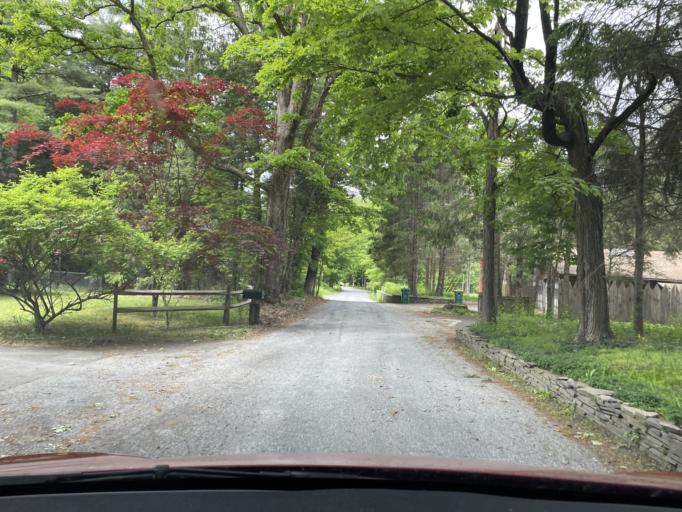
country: US
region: New York
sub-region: Ulster County
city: Woodstock
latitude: 42.0304
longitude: -74.1064
